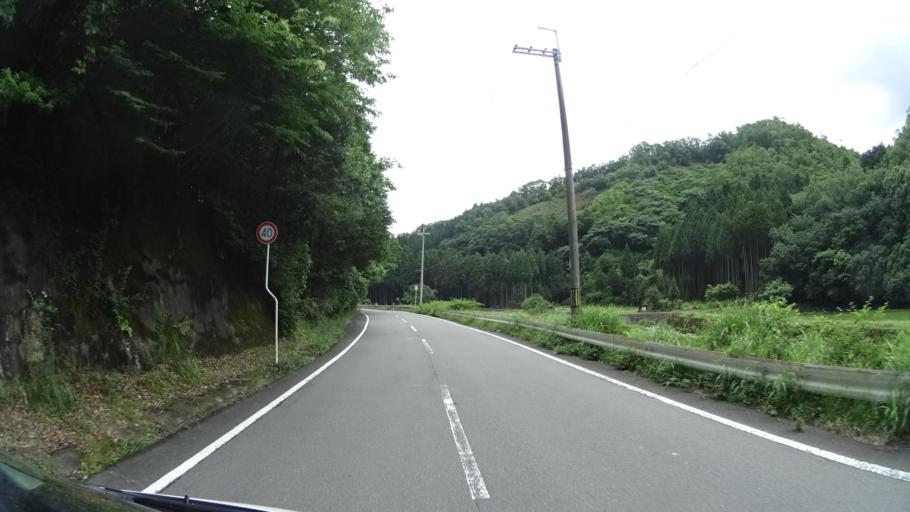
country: JP
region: Kyoto
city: Kameoka
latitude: 35.0730
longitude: 135.4102
